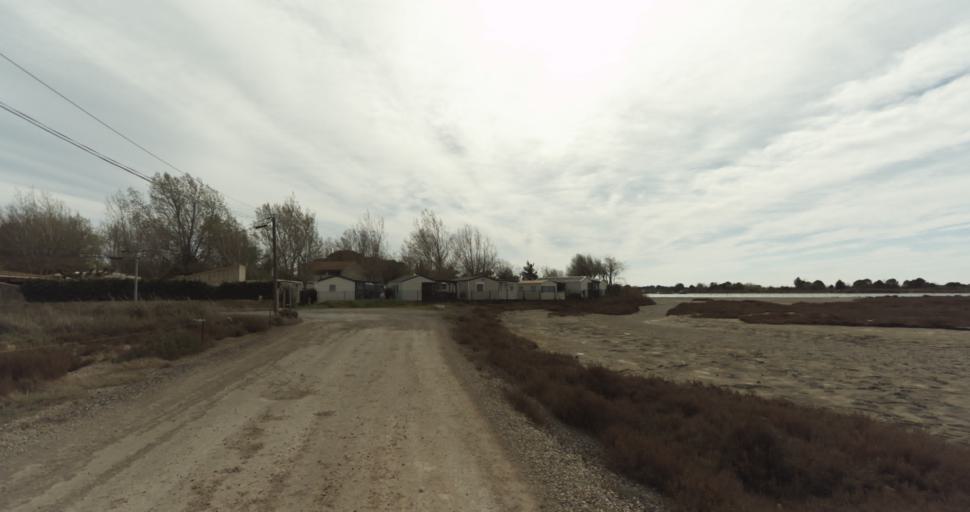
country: FR
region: Languedoc-Roussillon
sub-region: Departement de l'Herault
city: Marseillan
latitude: 43.3290
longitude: 3.5473
